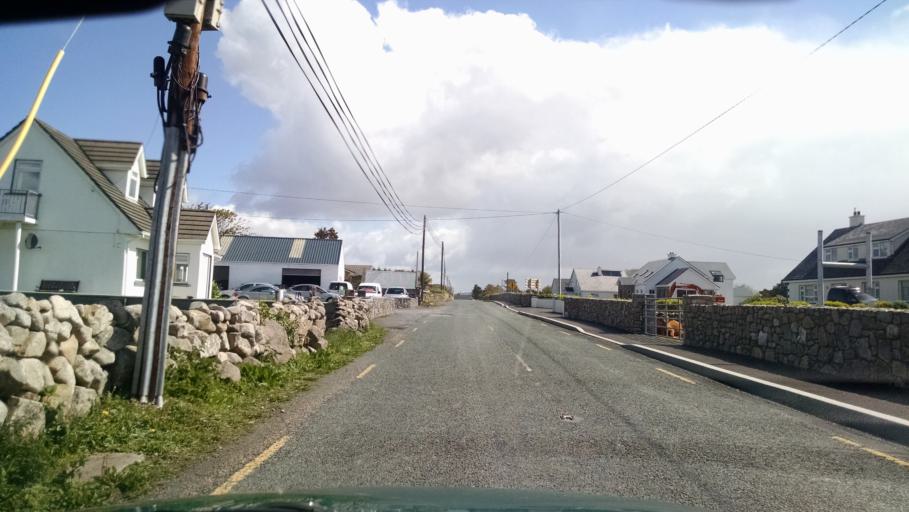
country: IE
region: Connaught
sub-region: County Galway
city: Oughterard
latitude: 53.2683
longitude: -9.5540
